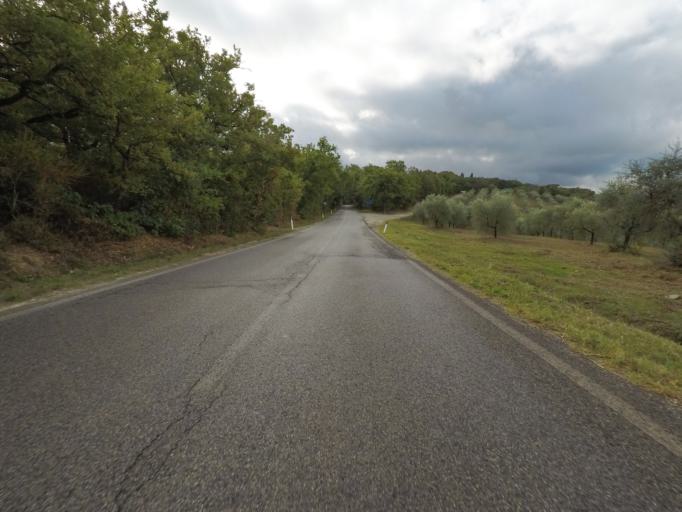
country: IT
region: Tuscany
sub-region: Provincia di Siena
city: Radda in Chianti
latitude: 43.4124
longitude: 11.3518
